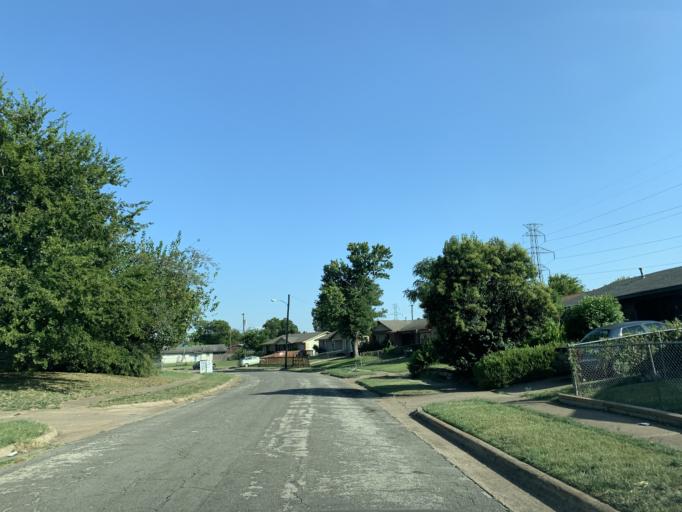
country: US
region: Texas
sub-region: Dallas County
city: Hutchins
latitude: 32.6618
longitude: -96.7681
